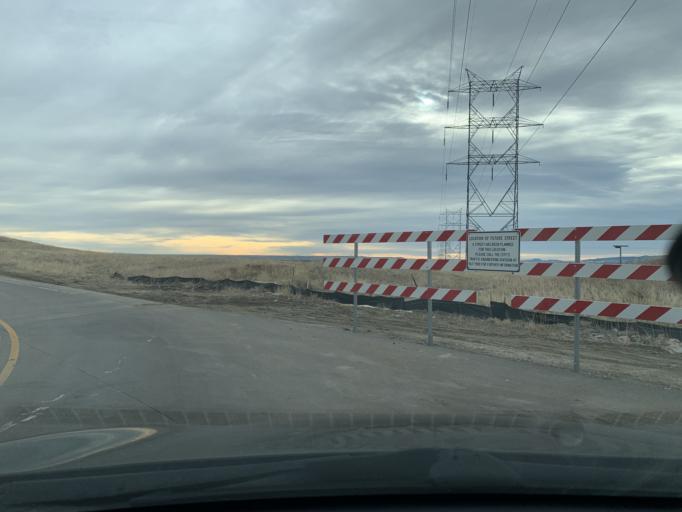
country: US
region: Colorado
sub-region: Jefferson County
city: West Pleasant View
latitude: 39.6676
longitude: -105.1771
